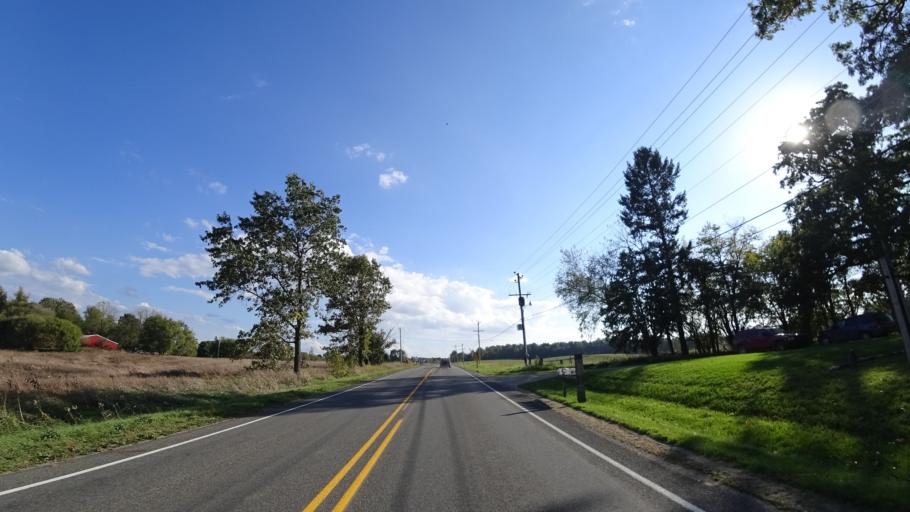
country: US
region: Michigan
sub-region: Saint Joseph County
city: Centreville
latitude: 41.8894
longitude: -85.5069
